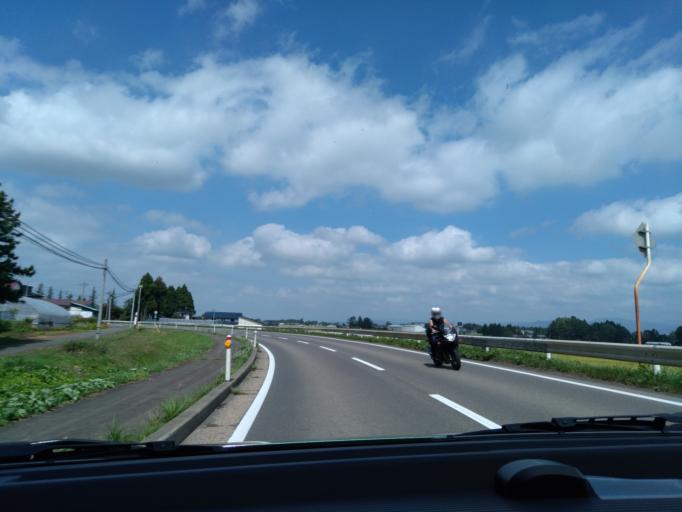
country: JP
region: Iwate
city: Hanamaki
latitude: 39.5307
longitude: 141.1132
